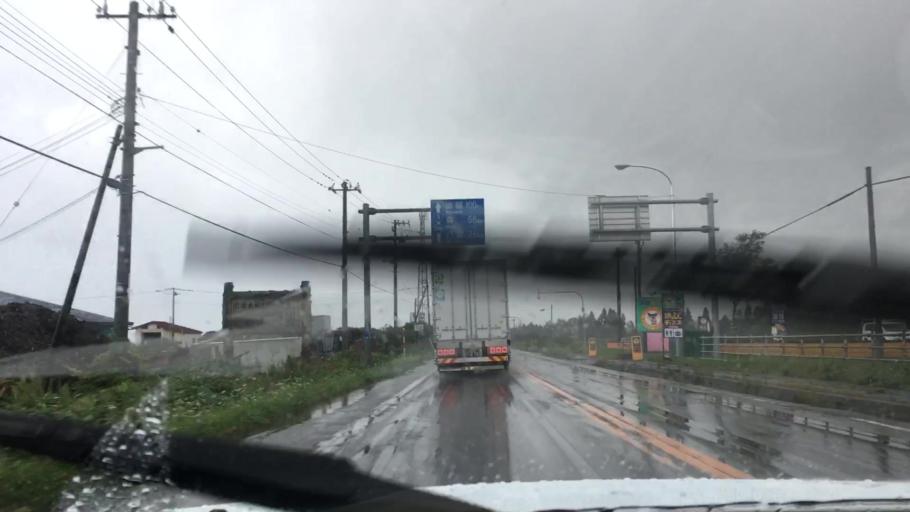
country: JP
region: Hokkaido
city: Niseko Town
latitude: 42.4745
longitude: 140.3462
